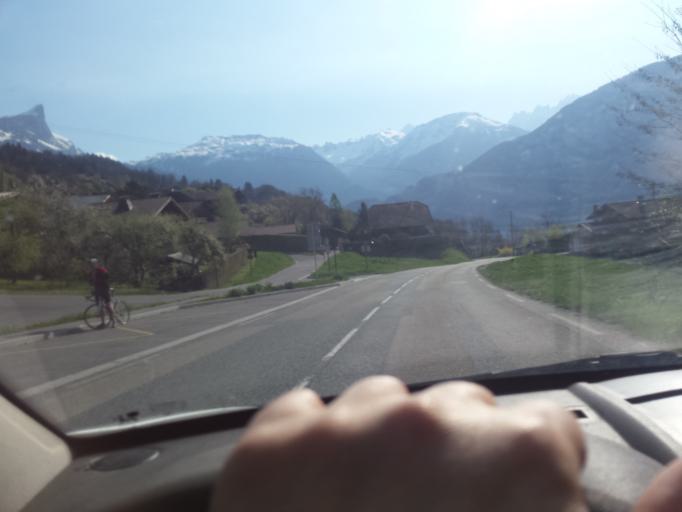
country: FR
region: Rhone-Alpes
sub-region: Departement de la Haute-Savoie
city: Passy
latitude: 45.9249
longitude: 6.6793
